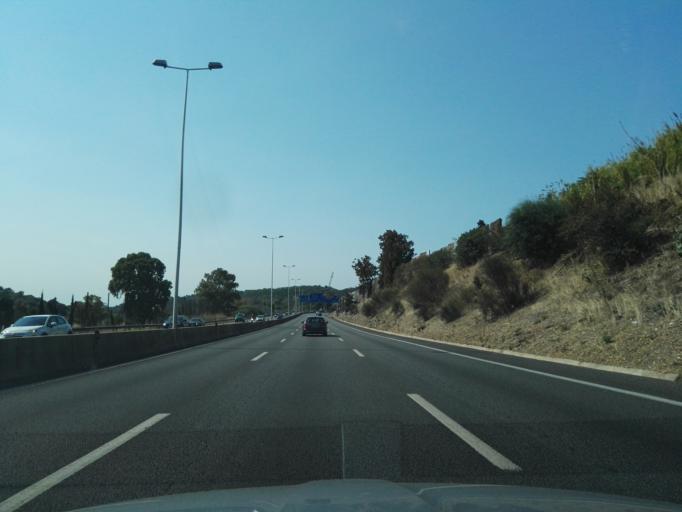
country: PT
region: Lisbon
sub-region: Oeiras
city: Linda-a-Velha
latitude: 38.7181
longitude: -9.2509
